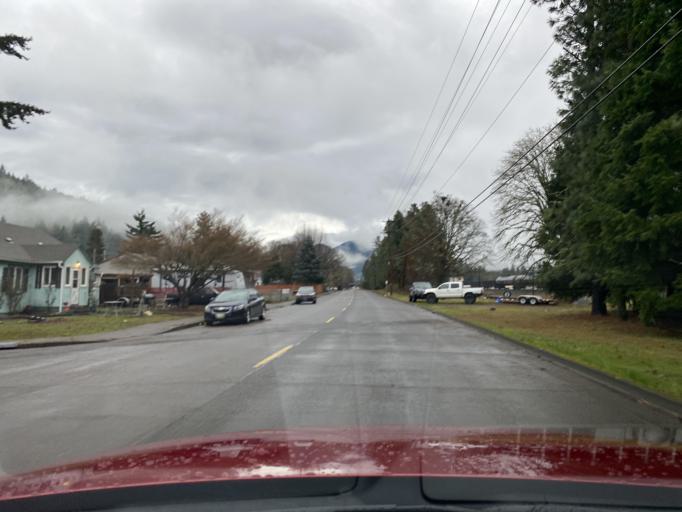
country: US
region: Oregon
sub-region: Lane County
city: Oakridge
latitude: 43.7475
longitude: -122.4763
